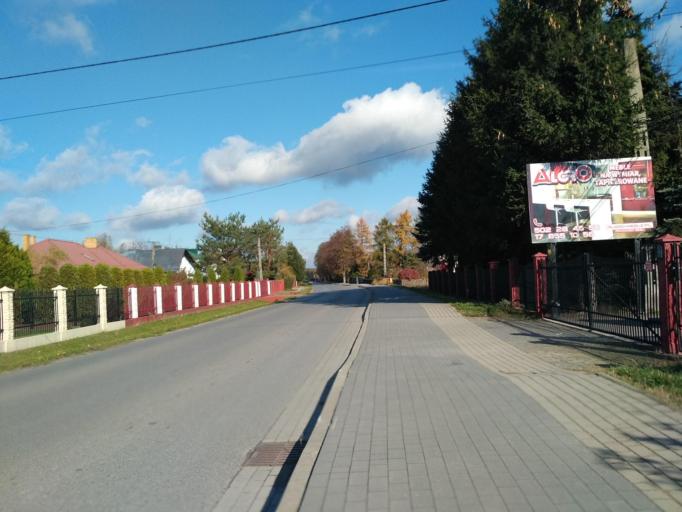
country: PL
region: Subcarpathian Voivodeship
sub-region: Powiat rzeszowski
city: Trzciana
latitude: 50.1109
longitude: 21.8581
